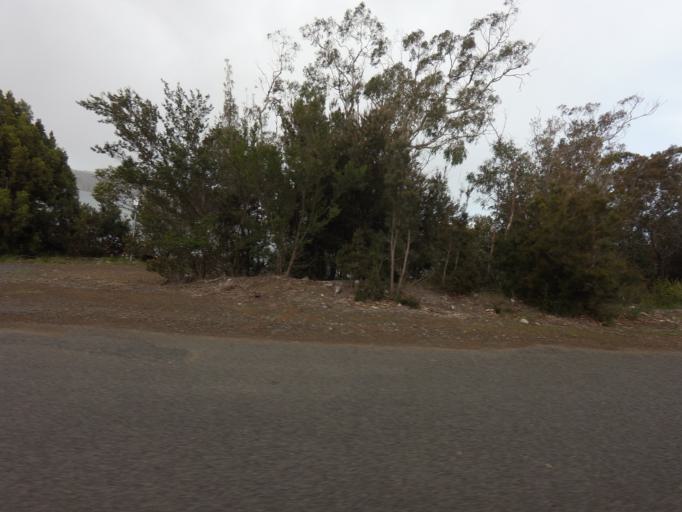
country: AU
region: Tasmania
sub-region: Sorell
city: Sorell
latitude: -42.5324
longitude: 147.9129
